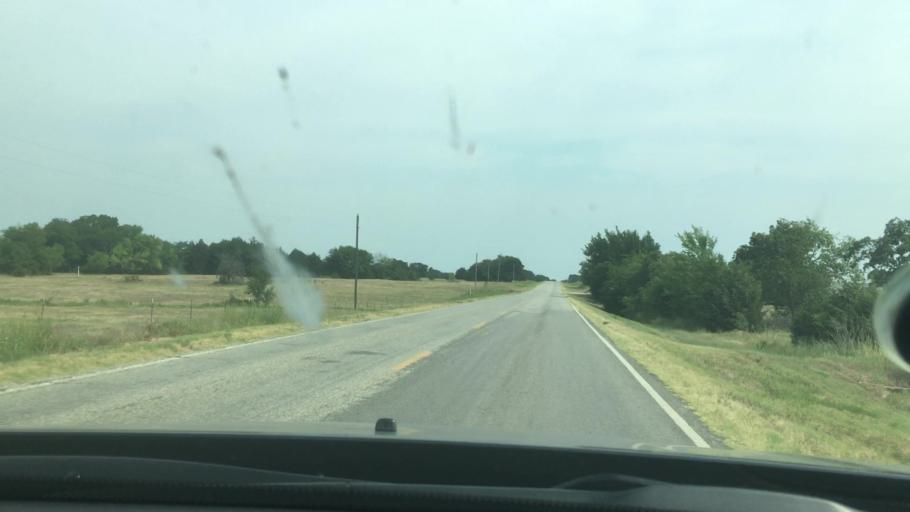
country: US
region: Oklahoma
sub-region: Johnston County
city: Tishomingo
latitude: 34.3077
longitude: -96.4247
